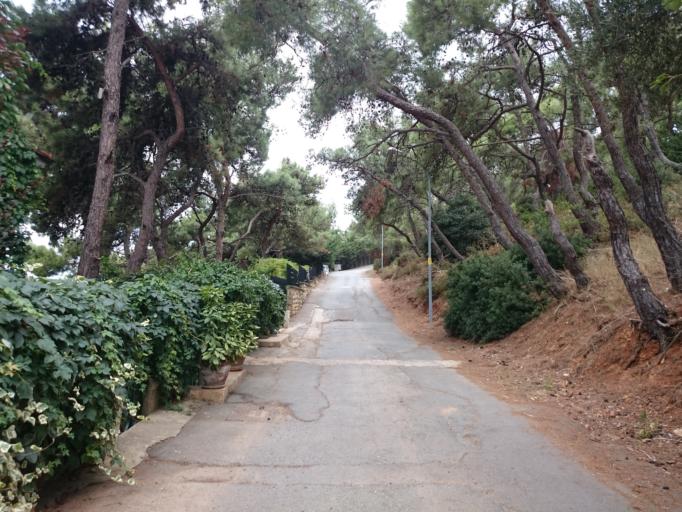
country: TR
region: Istanbul
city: Adalan
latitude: 40.8768
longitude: 29.0685
